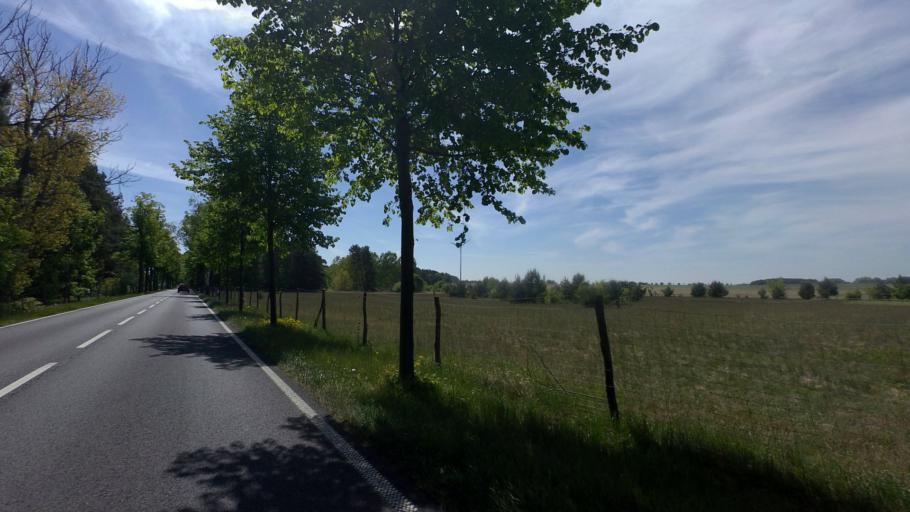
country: DE
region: Brandenburg
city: Luckenwalde
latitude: 52.1217
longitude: 13.1340
